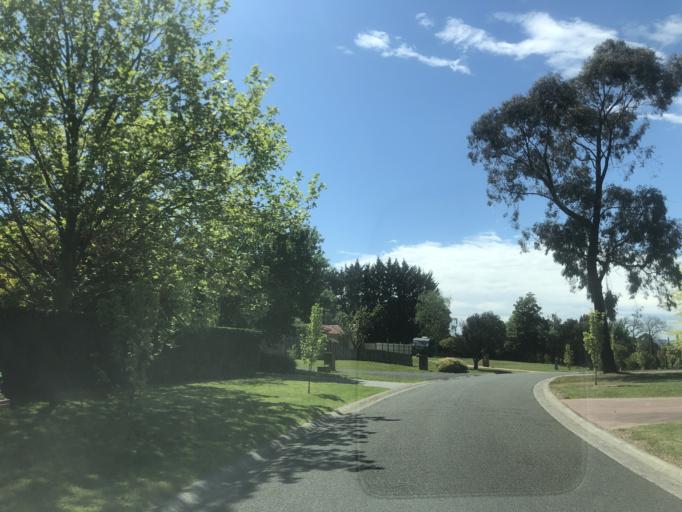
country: AU
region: Victoria
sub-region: Casey
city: Endeavour Hills
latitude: -37.9800
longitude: 145.2856
